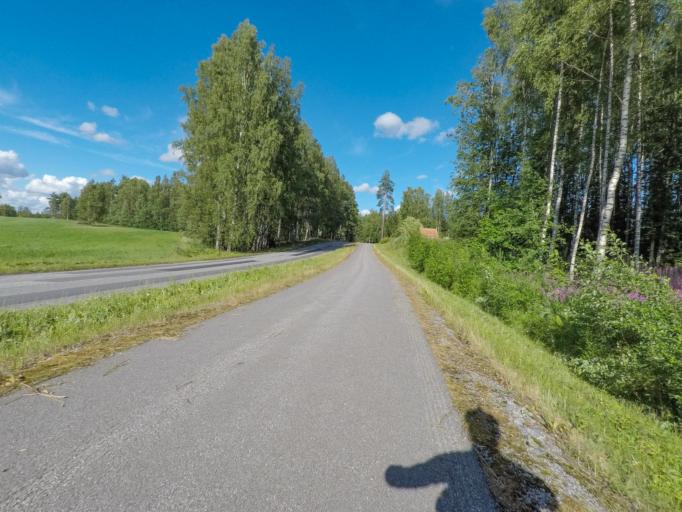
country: FI
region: South Karelia
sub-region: Lappeenranta
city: Joutseno
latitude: 61.1534
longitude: 28.5933
